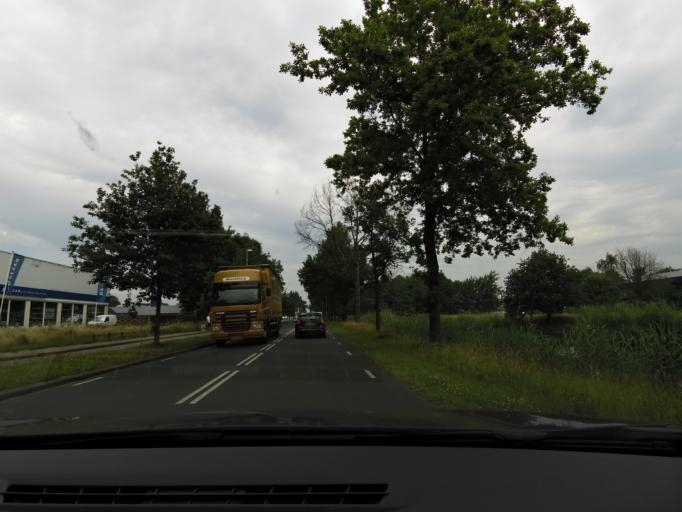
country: NL
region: Gelderland
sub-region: Gemeente Rheden
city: Spankeren
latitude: 52.0590
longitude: 6.1050
